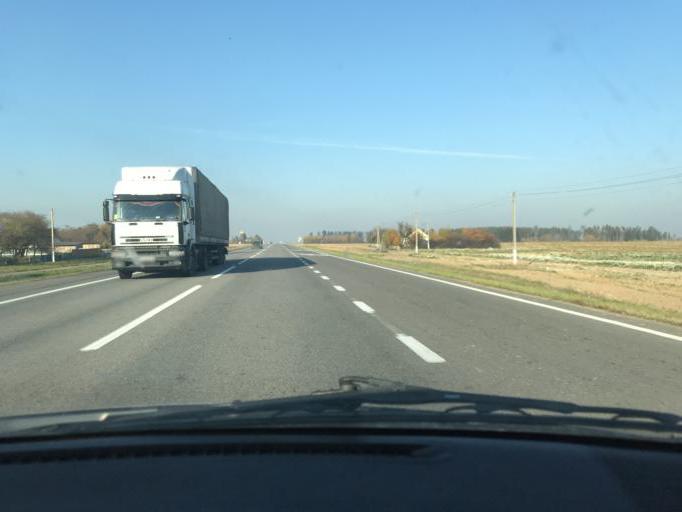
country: BY
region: Vitebsk
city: Orsha
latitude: 54.3385
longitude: 30.4462
